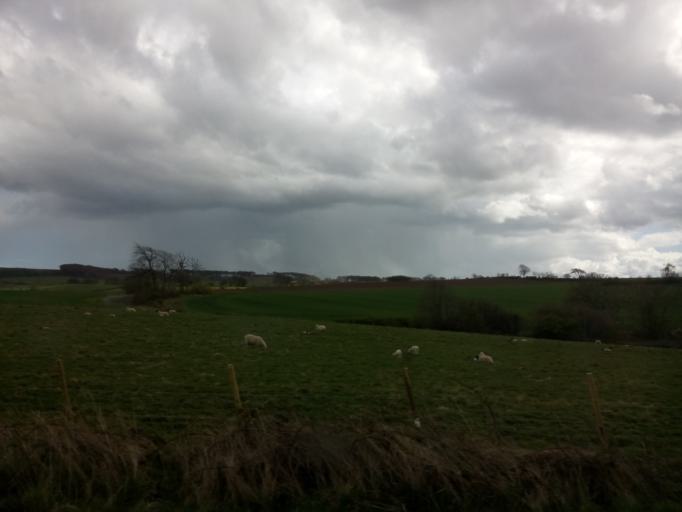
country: GB
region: Scotland
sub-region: The Scottish Borders
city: Eyemouth
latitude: 55.8314
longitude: -2.1223
